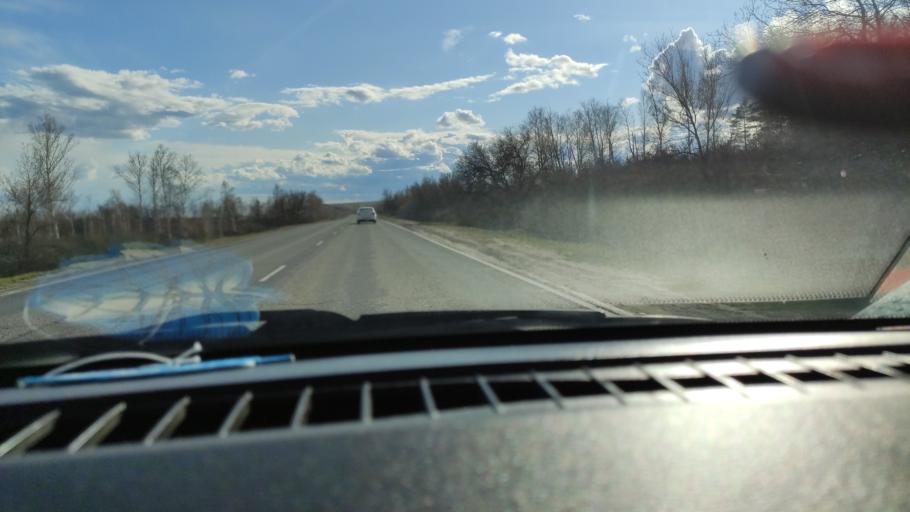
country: RU
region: Saratov
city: Sennoy
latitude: 52.1103
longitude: 46.8288
